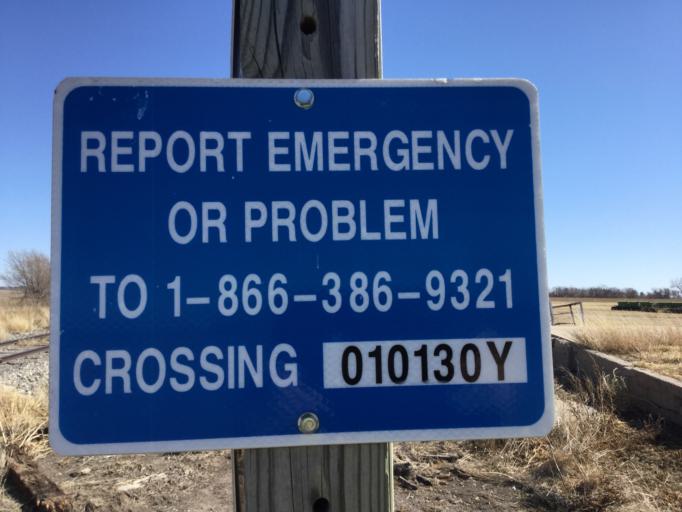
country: US
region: Kansas
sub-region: Pawnee County
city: Larned
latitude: 38.1662
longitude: -99.2165
